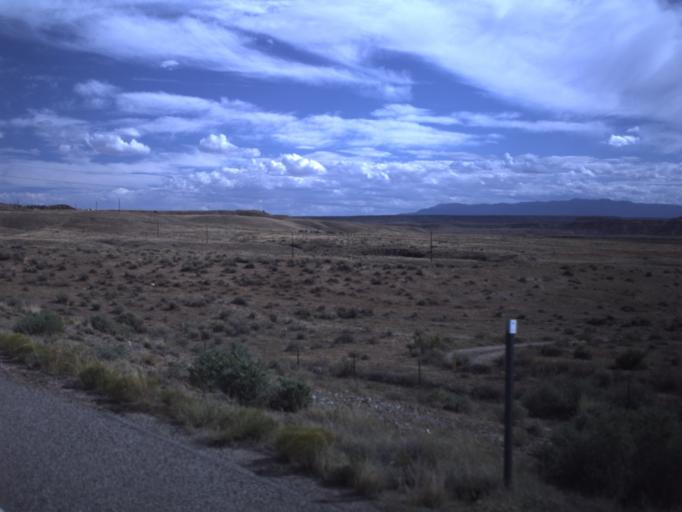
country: US
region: Colorado
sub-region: Montezuma County
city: Towaoc
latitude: 37.1979
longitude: -109.1505
